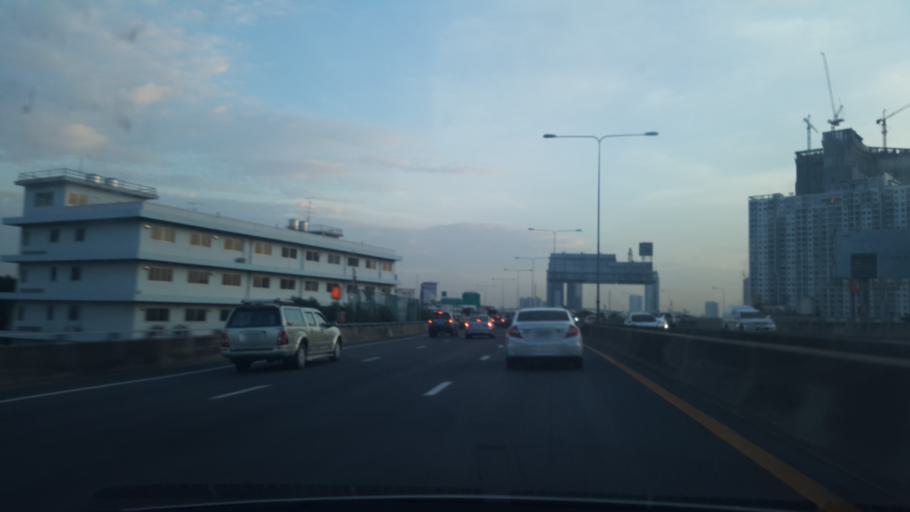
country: TH
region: Bangkok
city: Sathon
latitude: 13.7051
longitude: 100.5184
